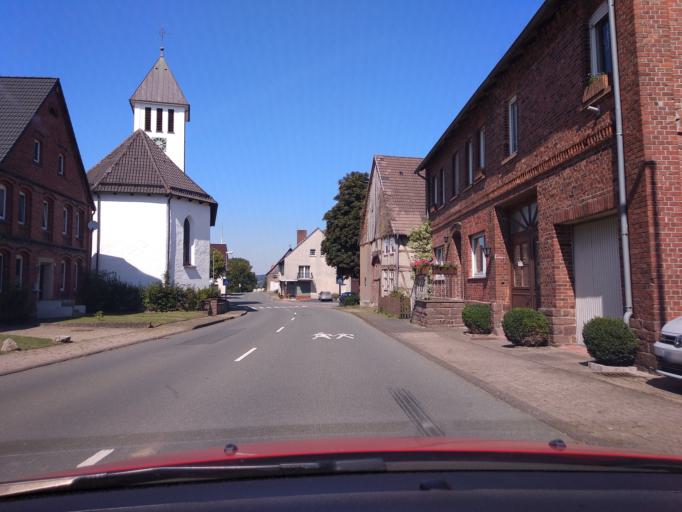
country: DE
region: North Rhine-Westphalia
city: Beverungen
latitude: 51.6816
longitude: 9.3110
